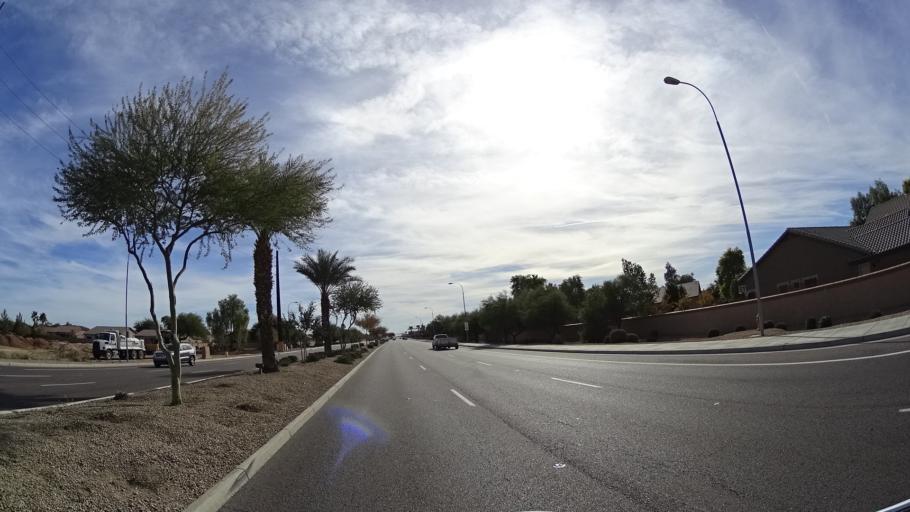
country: US
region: Arizona
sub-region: Maricopa County
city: Chandler
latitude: 33.2909
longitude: -111.8070
